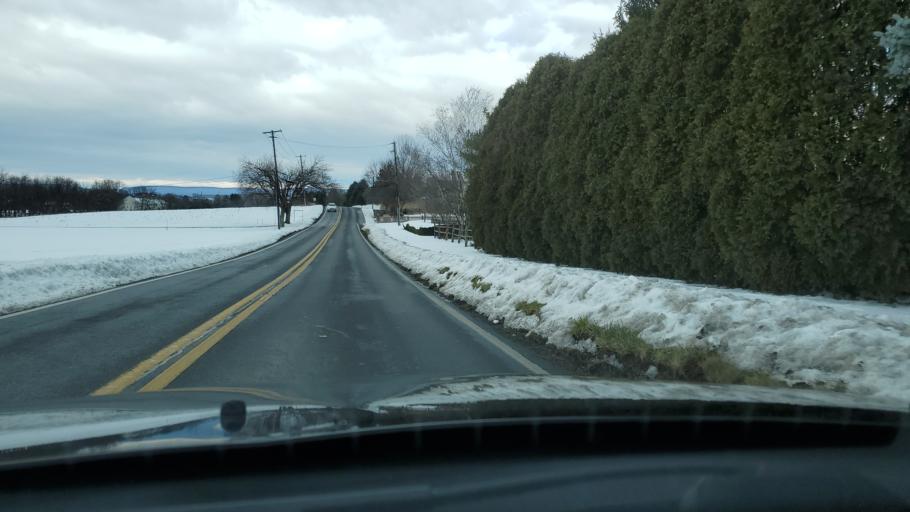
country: US
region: Pennsylvania
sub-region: Cumberland County
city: Mechanicsburg
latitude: 40.2105
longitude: -77.0388
